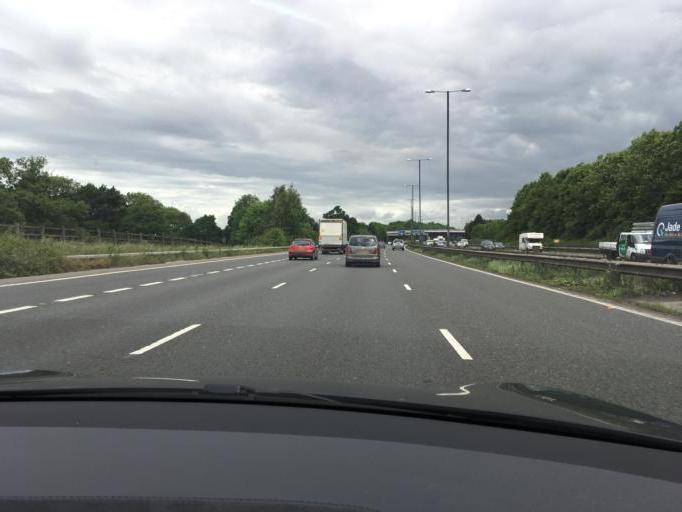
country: GB
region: England
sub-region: Manchester
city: Ringway
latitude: 53.3690
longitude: -2.2930
